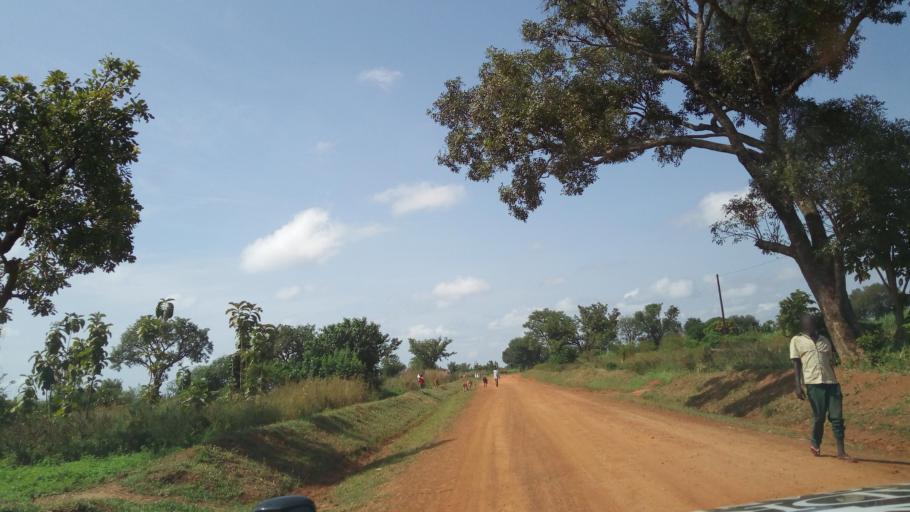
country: UG
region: Northern Region
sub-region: Moyo District
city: Moyo
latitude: 3.5815
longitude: 31.5194
